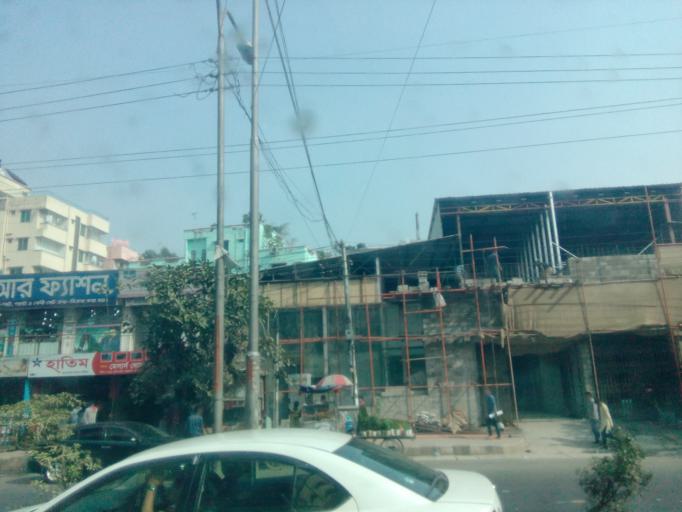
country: BD
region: Dhaka
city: Paltan
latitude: 23.7917
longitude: 90.4248
